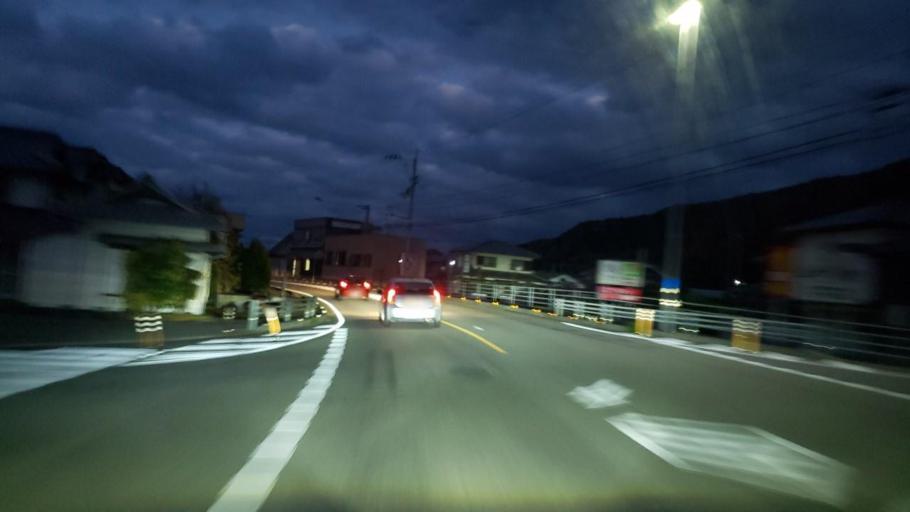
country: JP
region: Tokushima
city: Narutocho-mitsuishi
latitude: 34.2137
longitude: 134.4815
